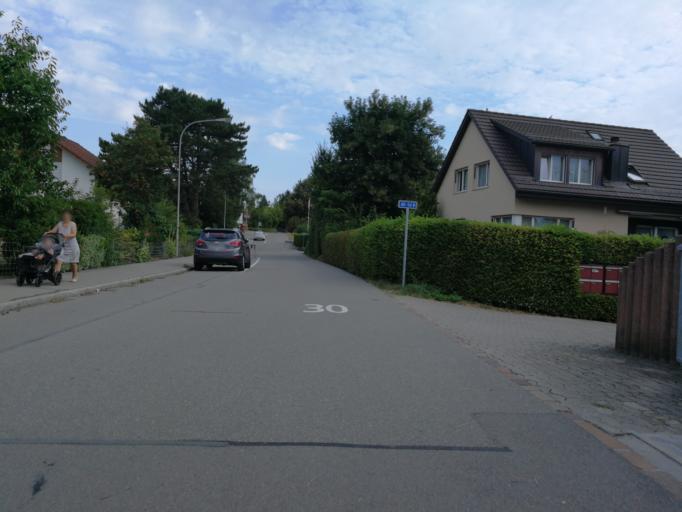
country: CH
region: Zurich
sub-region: Bezirk Uster
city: Monchaltorf
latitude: 47.3113
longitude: 8.7243
